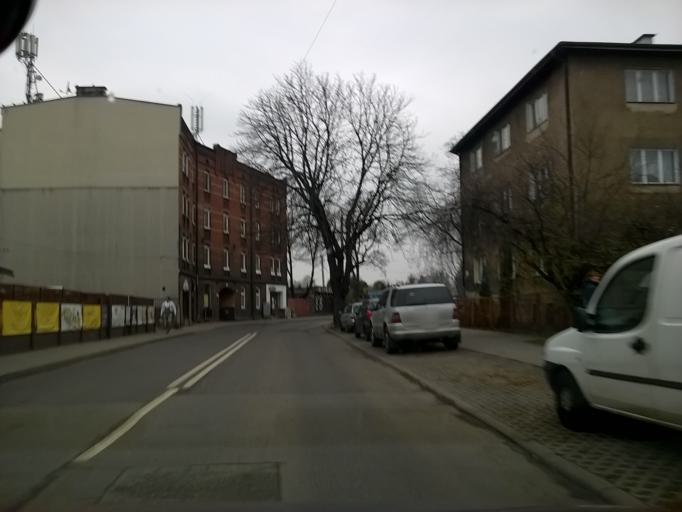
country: PL
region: Silesian Voivodeship
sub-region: Chorzow
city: Chorzow
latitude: 50.2833
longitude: 18.9532
